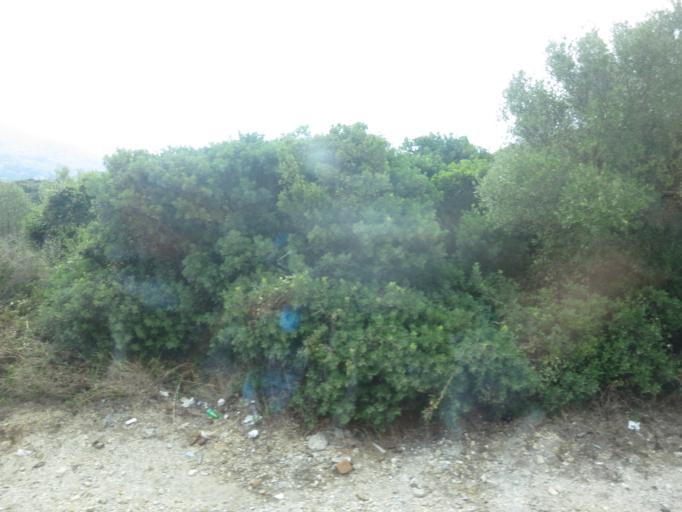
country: ES
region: Andalusia
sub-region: Provincia de Cadiz
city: Tarifa
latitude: 36.0627
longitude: -5.5361
